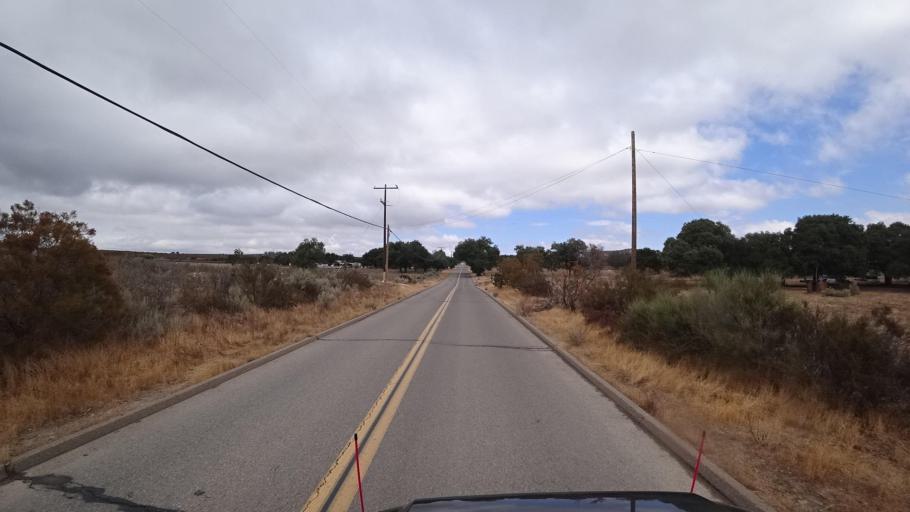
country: MX
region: Baja California
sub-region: Tecate
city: Cereso del Hongo
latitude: 32.6129
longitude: -116.3203
